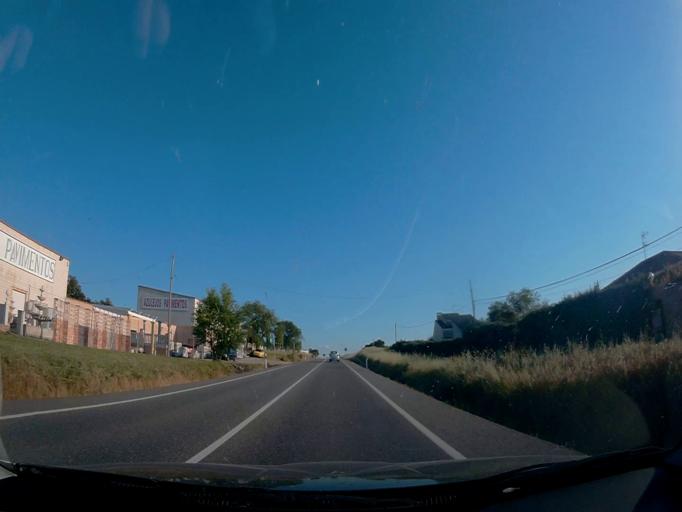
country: ES
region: Castille-La Mancha
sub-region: Province of Toledo
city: Escalona
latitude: 40.1320
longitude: -4.4049
